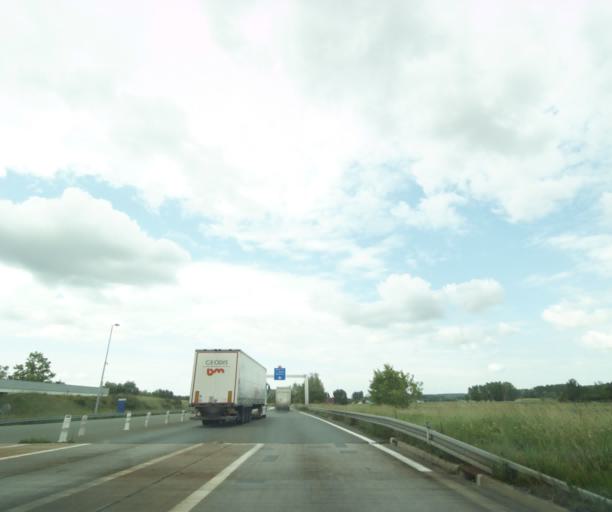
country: FR
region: Pays de la Loire
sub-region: Departement de Maine-et-Loire
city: Vivy
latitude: 47.3106
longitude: -0.0315
